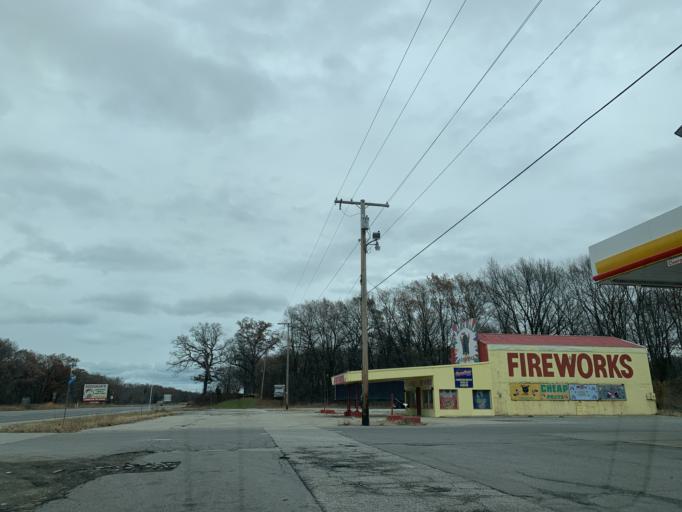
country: US
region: Indiana
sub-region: LaPorte County
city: Long Beach
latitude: 41.7582
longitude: -86.8029
